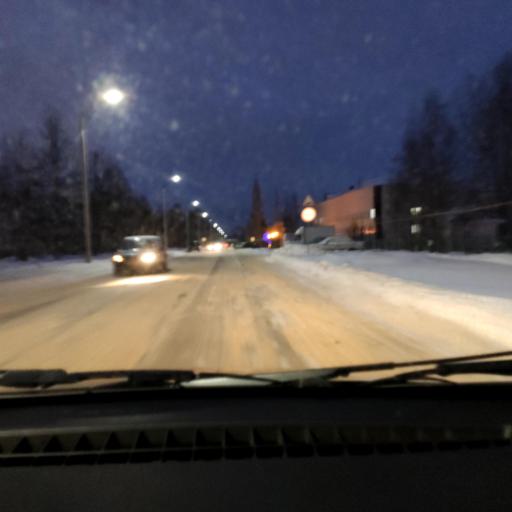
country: RU
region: Bashkortostan
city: Blagoveshchensk
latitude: 55.0478
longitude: 55.9483
